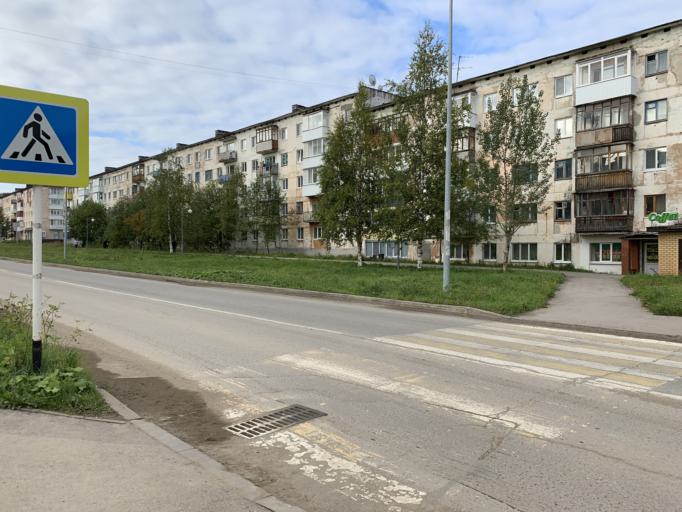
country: RU
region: Perm
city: Gubakha
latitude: 58.8289
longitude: 57.5579
